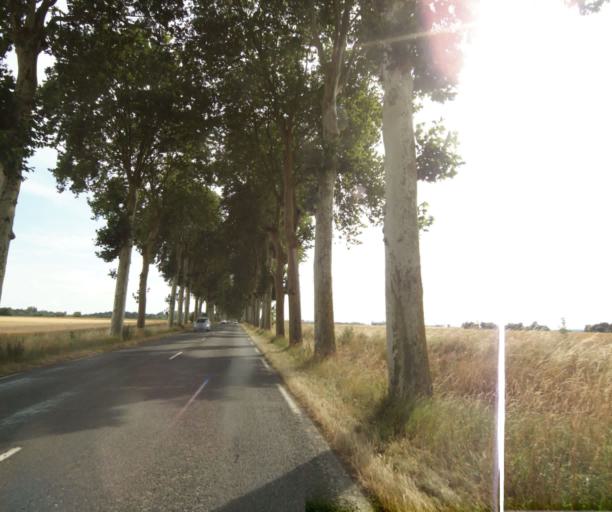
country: FR
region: Ile-de-France
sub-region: Departement de Seine-et-Marne
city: La Chapelle-la-Reine
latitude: 48.3318
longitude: 2.5900
